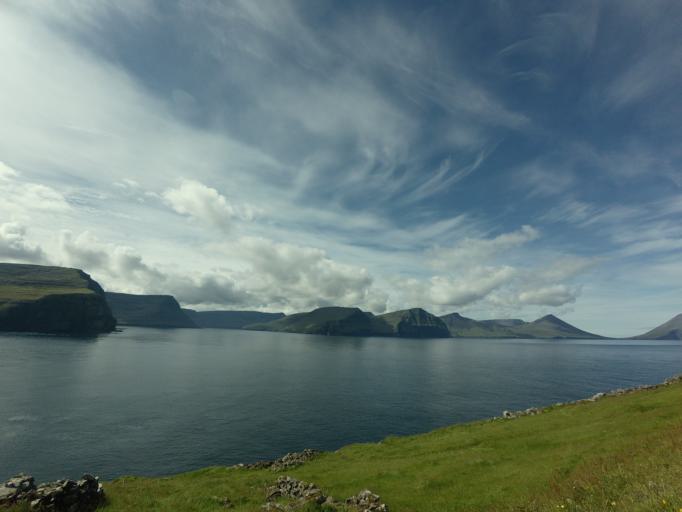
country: FO
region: Nordoyar
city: Klaksvik
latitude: 62.3213
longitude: -6.3248
